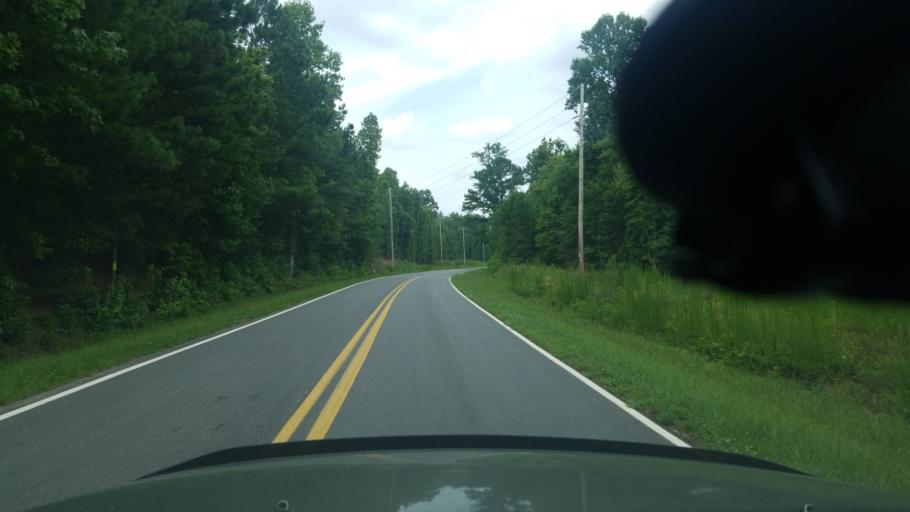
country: US
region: Georgia
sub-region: Dawson County
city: Dawsonville
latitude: 34.3228
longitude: -84.1947
